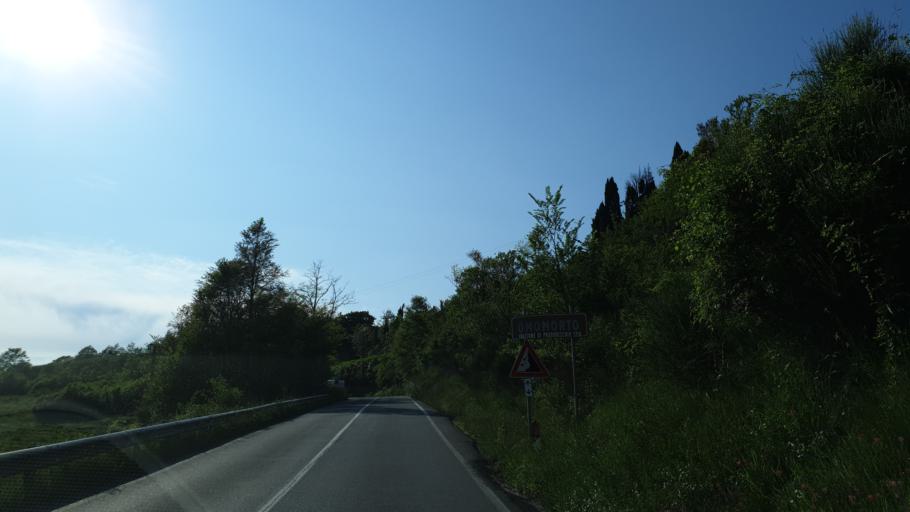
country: IT
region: Tuscany
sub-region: Province of Arezzo
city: Stia
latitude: 43.7812
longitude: 11.6646
